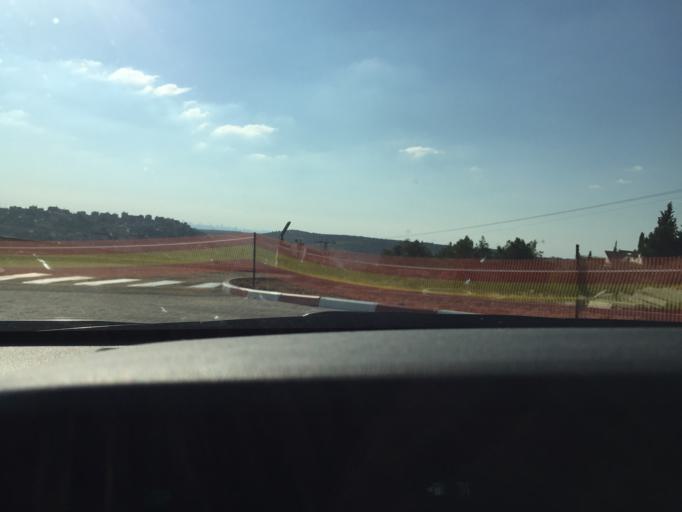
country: PS
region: West Bank
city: Al Lubban al Gharbi
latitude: 32.0339
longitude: 35.0504
